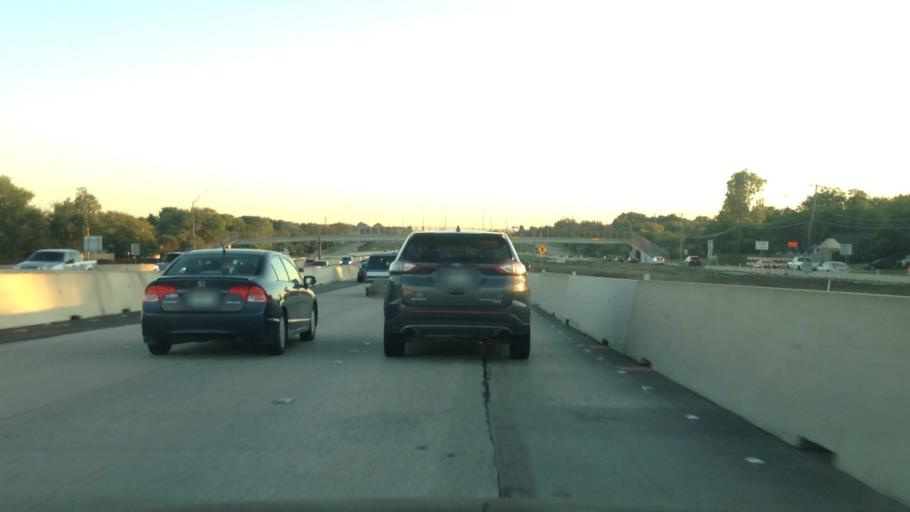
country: US
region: Texas
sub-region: Tarrant County
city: Arlington
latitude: 32.7325
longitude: -97.0628
